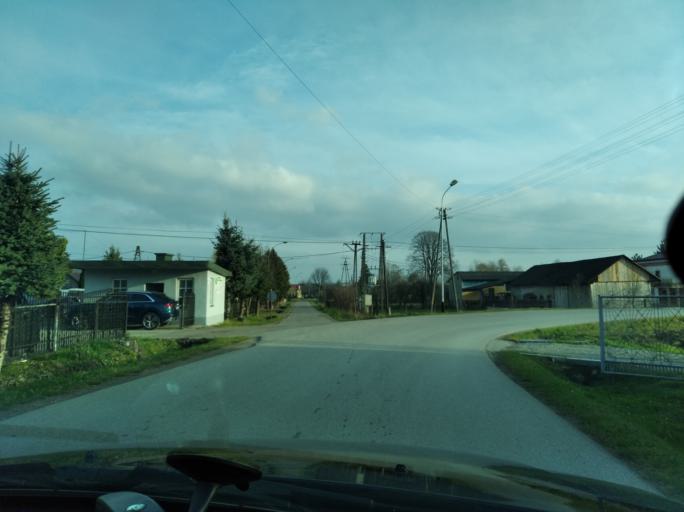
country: PL
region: Subcarpathian Voivodeship
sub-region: Powiat przemyski
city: Przedmiescie Dubieckie
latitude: 49.8316
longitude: 22.3730
